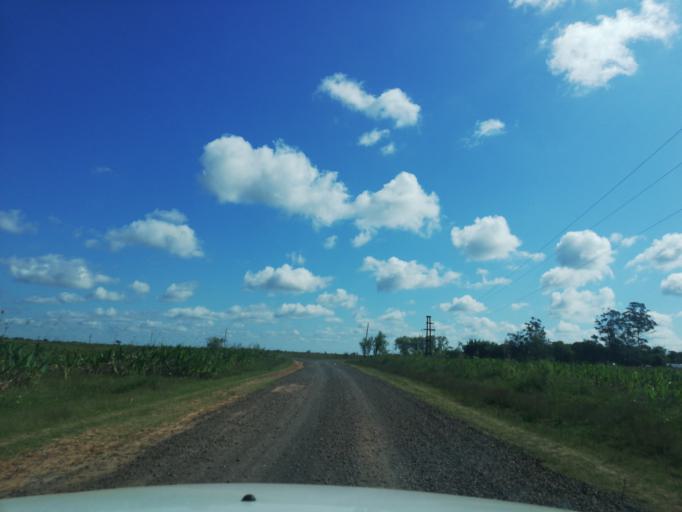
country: AR
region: Corrientes
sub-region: Departamento de San Miguel
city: San Miguel
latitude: -27.9829
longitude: -57.5816
